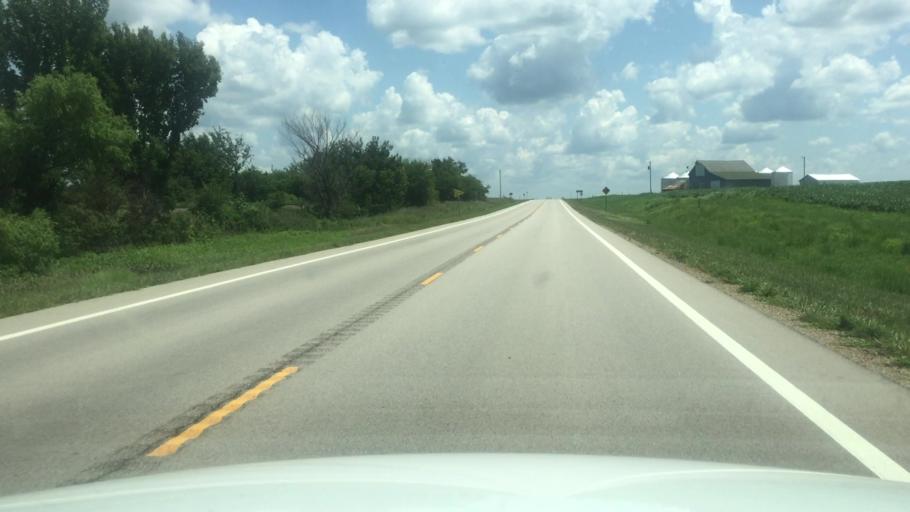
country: US
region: Kansas
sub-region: Brown County
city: Horton
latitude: 39.6538
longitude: -95.3662
